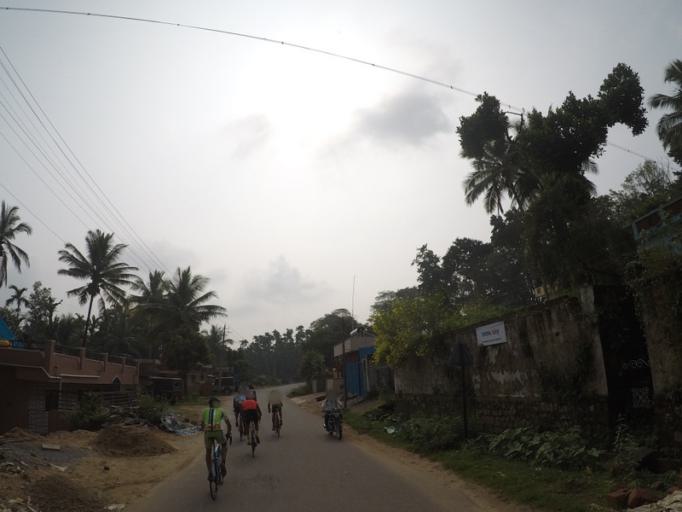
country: IN
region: Karnataka
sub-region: Chikmagalur
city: Koppa
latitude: 13.3481
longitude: 75.4706
